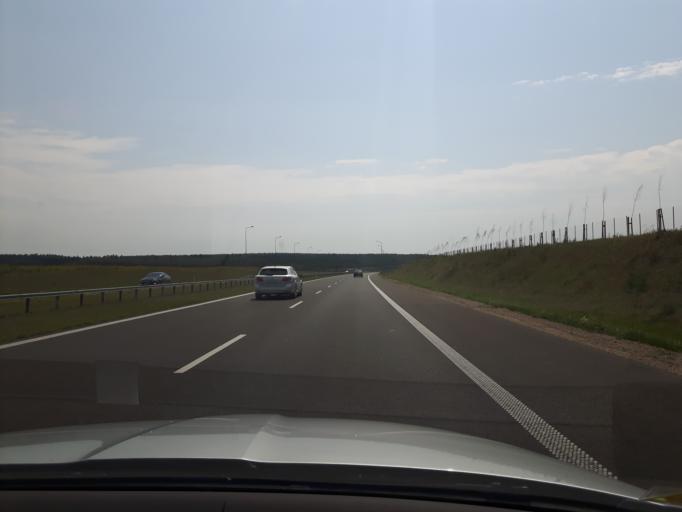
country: PL
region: Warmian-Masurian Voivodeship
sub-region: Powiat nidzicki
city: Nidzica
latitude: 53.2838
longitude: 20.4386
